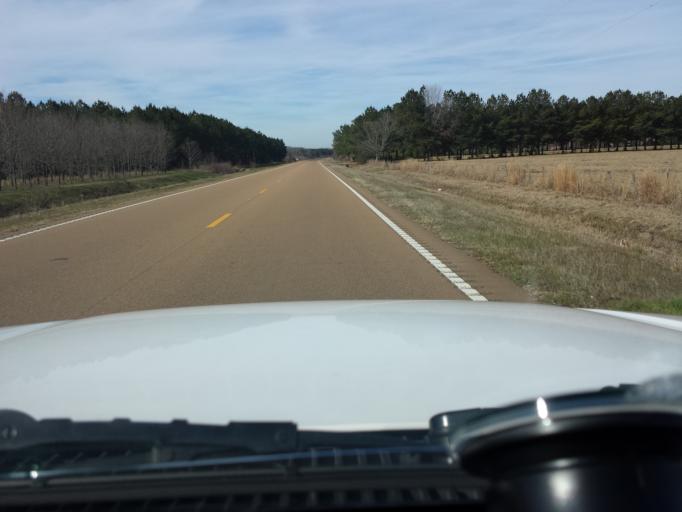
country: US
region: Mississippi
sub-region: Madison County
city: Canton
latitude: 32.6971
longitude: -90.0784
